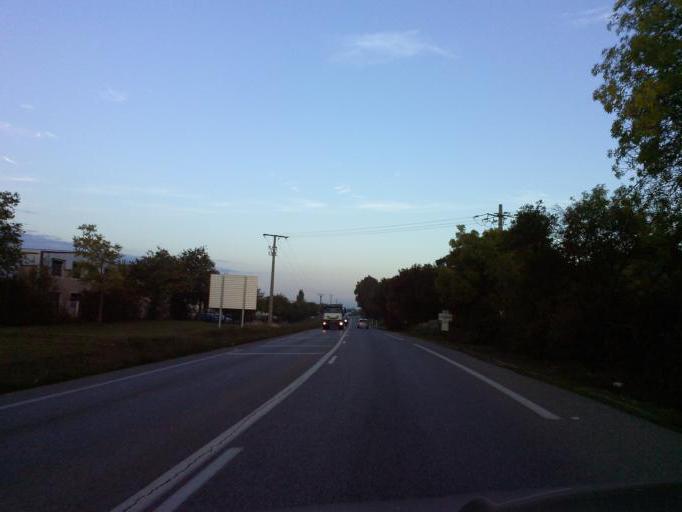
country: FR
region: Provence-Alpes-Cote d'Azur
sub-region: Departement des Bouches-du-Rhone
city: Saint-Cannat
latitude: 43.6136
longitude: 5.3222
